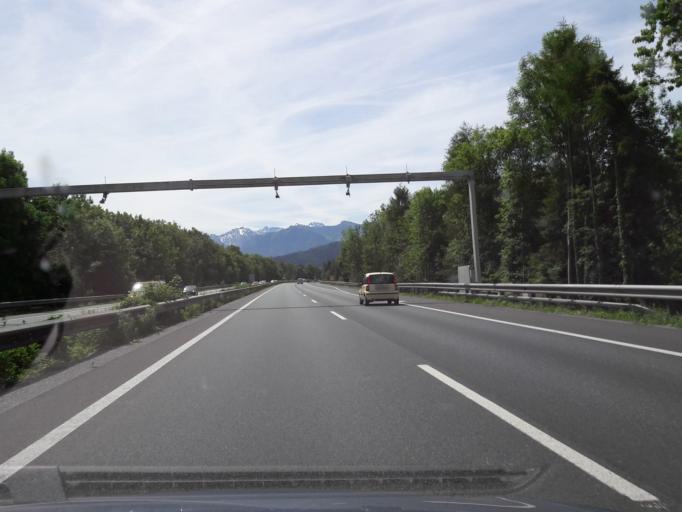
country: AT
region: Vorarlberg
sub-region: Politischer Bezirk Feldkirch
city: Klaus
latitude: 47.2969
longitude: 9.6252
